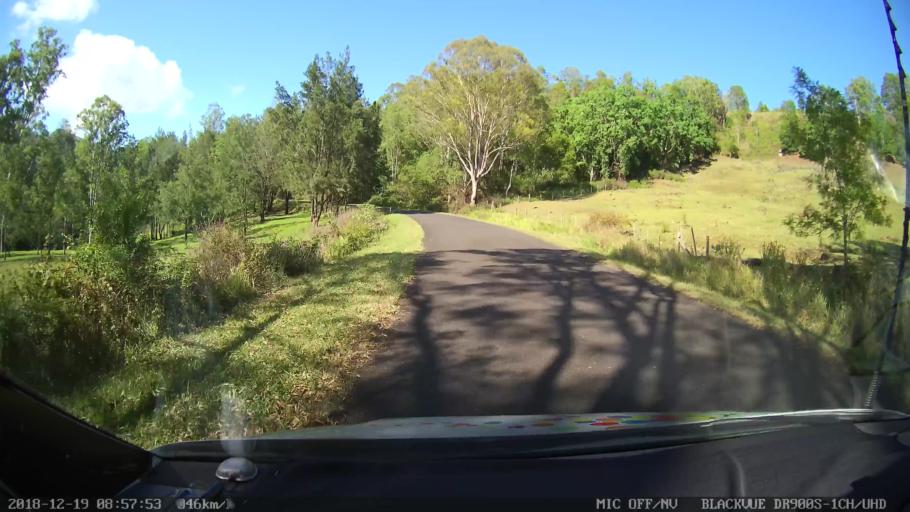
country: AU
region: New South Wales
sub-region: Kyogle
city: Kyogle
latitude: -28.4217
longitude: 152.9684
